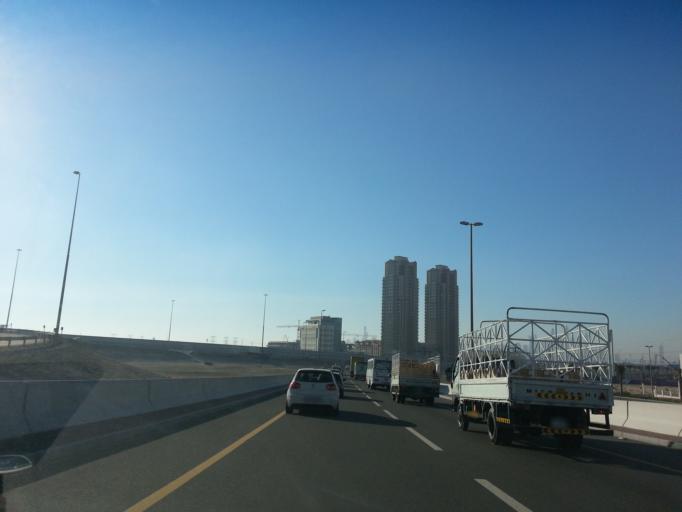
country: AE
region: Dubai
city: Dubai
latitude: 25.0452
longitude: 55.2012
